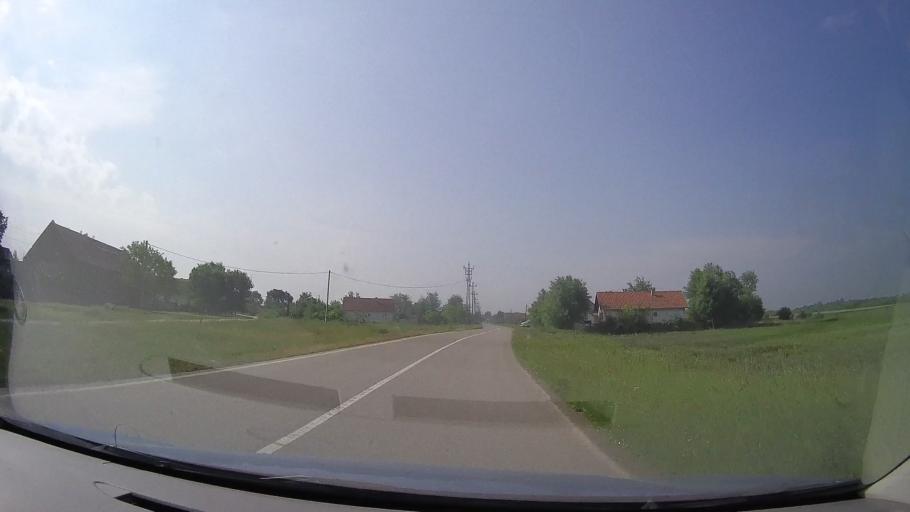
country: RS
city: Jasa Tomic
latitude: 45.4564
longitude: 20.8557
